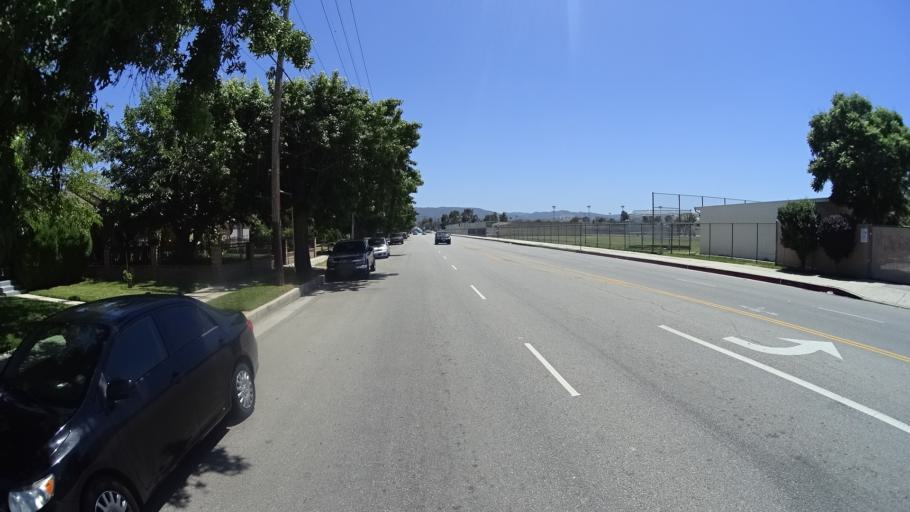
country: US
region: California
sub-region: Los Angeles County
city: Northridge
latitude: 34.1900
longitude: -118.5273
